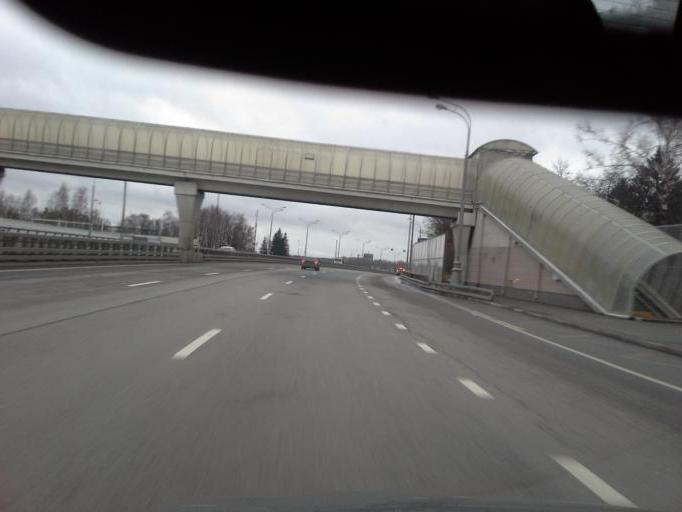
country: RU
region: Moskovskaya
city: Annino
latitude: 55.5975
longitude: 37.2421
